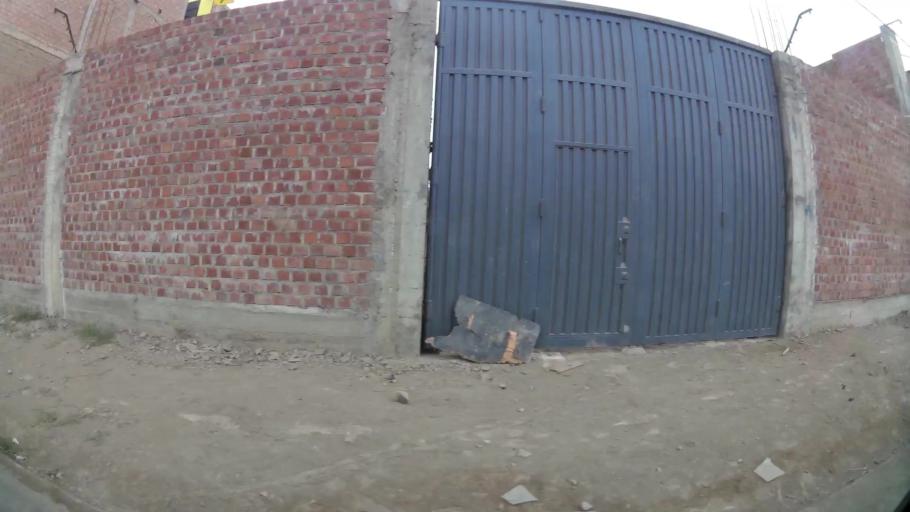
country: PE
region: Lima
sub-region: Lima
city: Independencia
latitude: -11.9723
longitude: -77.0910
